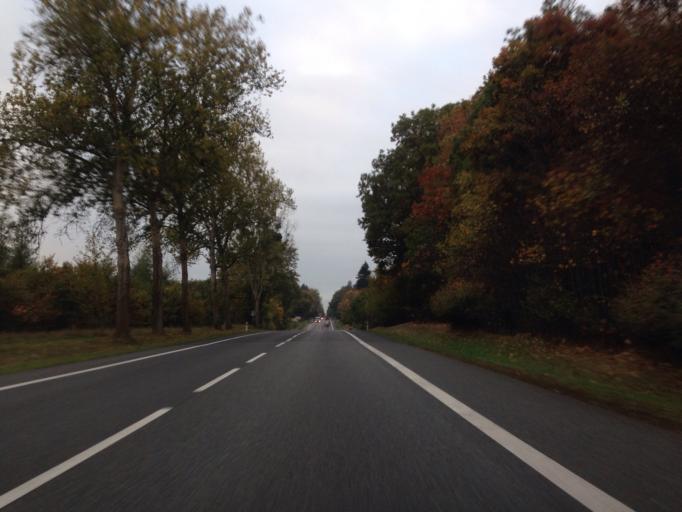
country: PL
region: Kujawsko-Pomorskie
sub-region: Powiat swiecki
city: Jezewo
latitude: 53.4494
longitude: 18.5710
